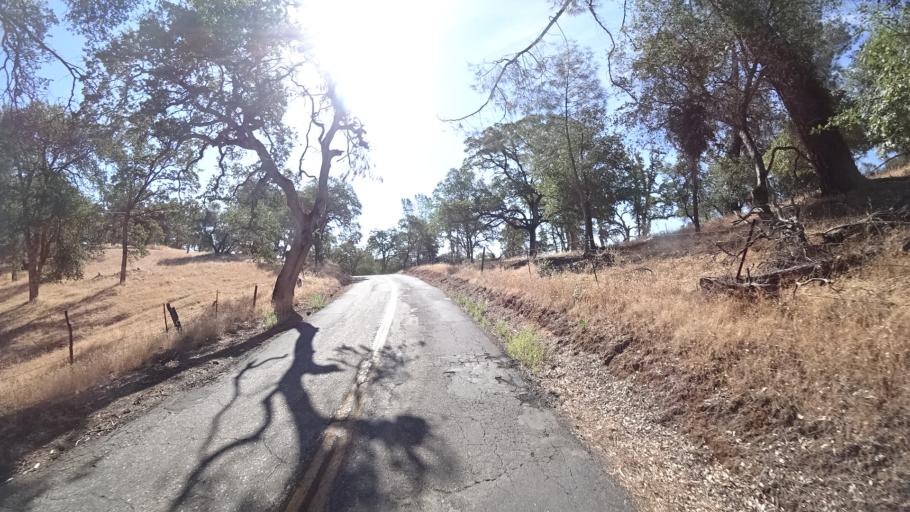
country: US
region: California
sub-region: Calaveras County
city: Mountain Ranch
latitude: 38.1548
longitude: -120.5802
